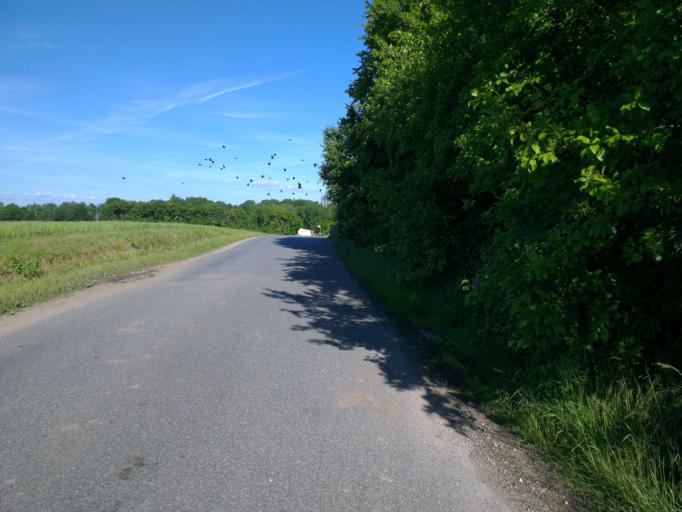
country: DK
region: Capital Region
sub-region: Frederikssund Kommune
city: Skibby
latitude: 55.7671
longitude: 11.9591
